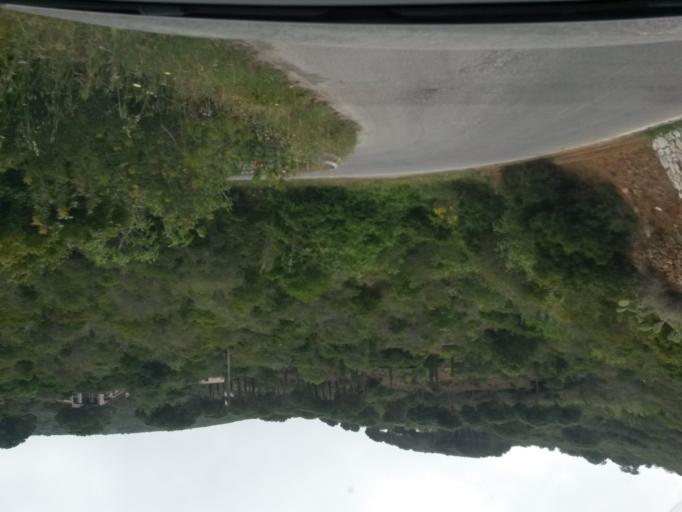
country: IT
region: Tuscany
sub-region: Provincia di Livorno
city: Capoliveri
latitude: 42.7381
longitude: 10.3778
